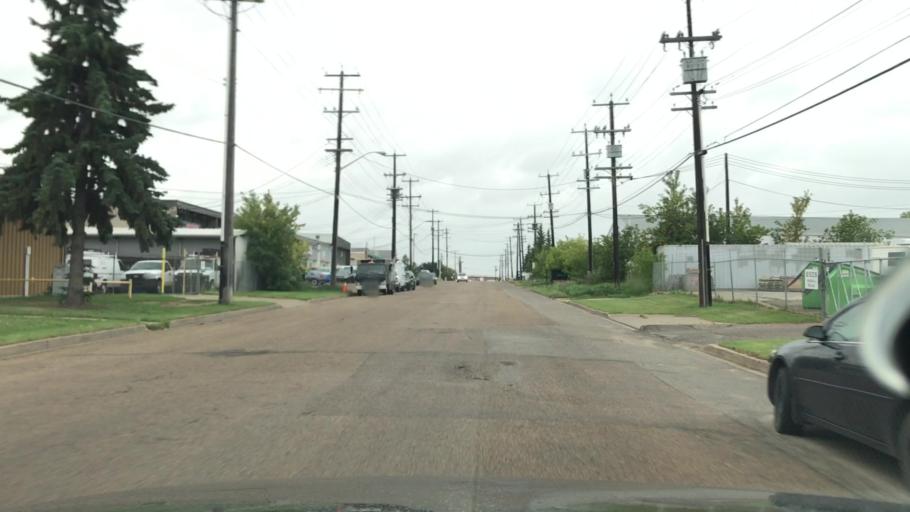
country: CA
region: Alberta
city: Edmonton
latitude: 53.5013
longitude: -113.4544
